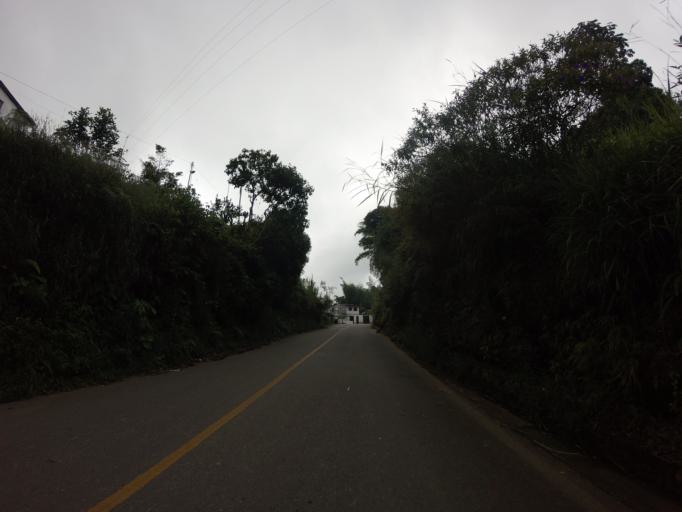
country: CO
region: Caldas
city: Marquetalia
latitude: 5.3079
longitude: -75.0049
